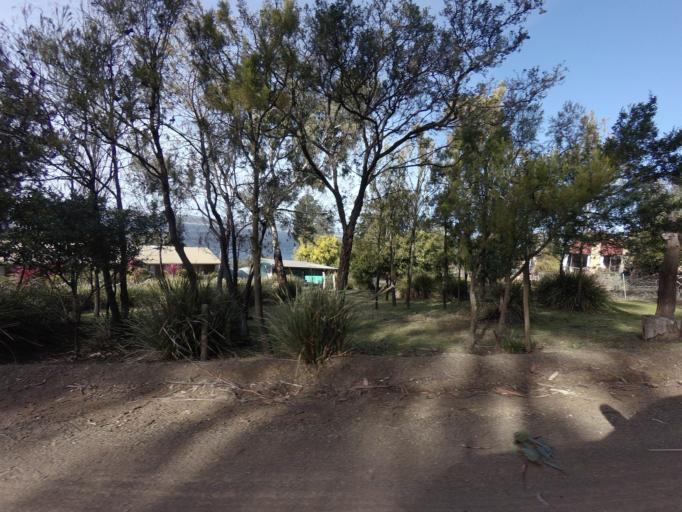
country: AU
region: Tasmania
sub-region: Kingborough
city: Kettering
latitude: -43.1178
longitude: 147.2701
